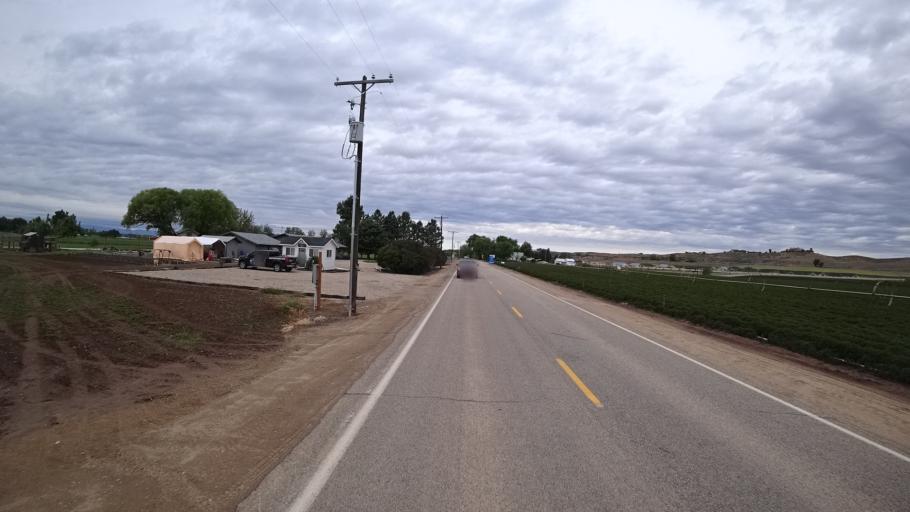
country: US
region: Idaho
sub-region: Ada County
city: Star
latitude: 43.7212
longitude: -116.4798
